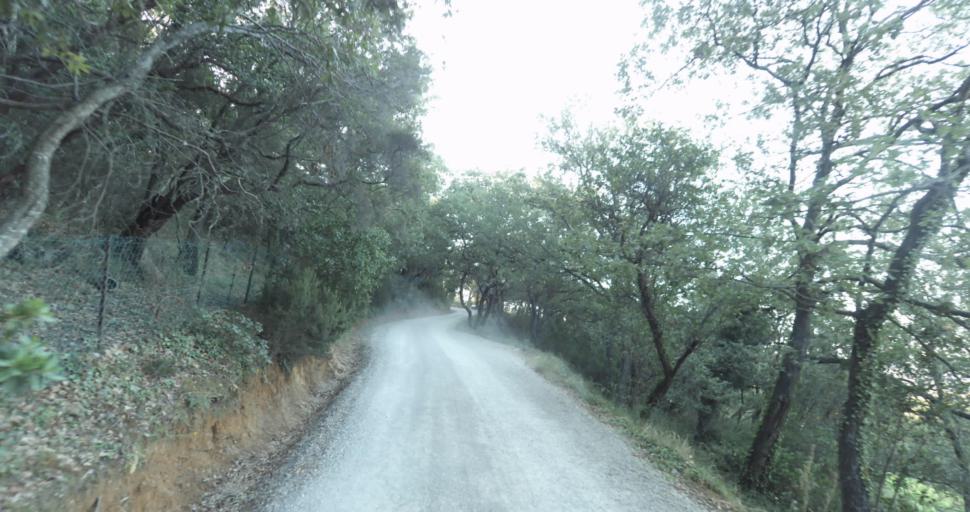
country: FR
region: Provence-Alpes-Cote d'Azur
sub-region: Departement du Var
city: Gassin
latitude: 43.2264
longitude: 6.5912
